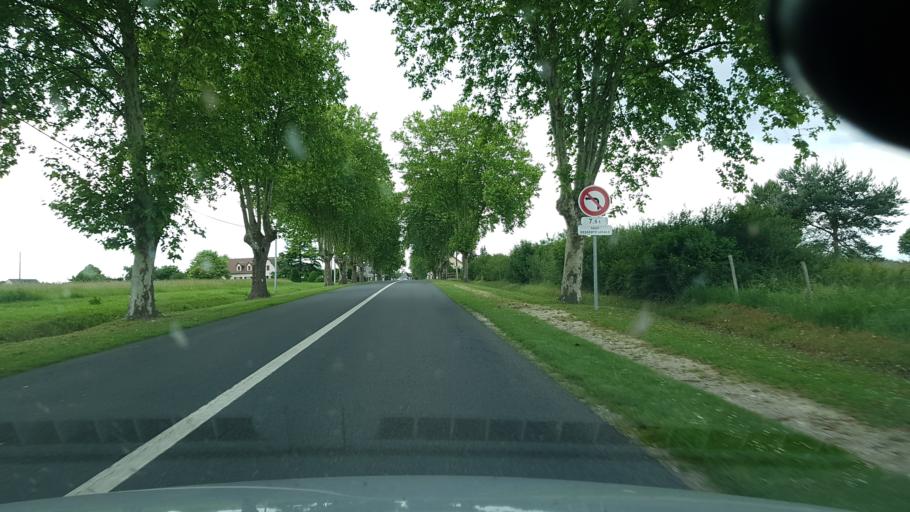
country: FR
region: Centre
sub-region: Departement du Loir-et-Cher
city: Chatillon-sur-Cher
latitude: 47.3387
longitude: 1.4828
